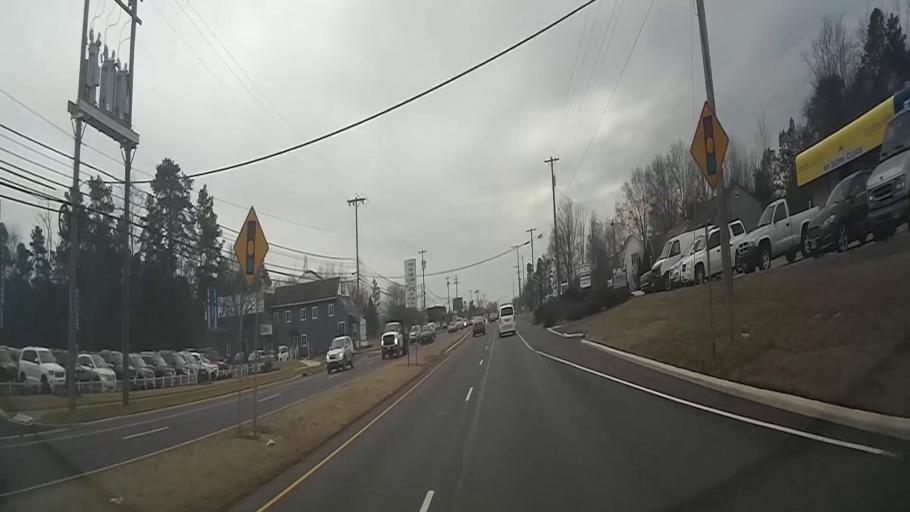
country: US
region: New Jersey
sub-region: Camden County
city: Berlin
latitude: 39.8277
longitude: -74.9274
